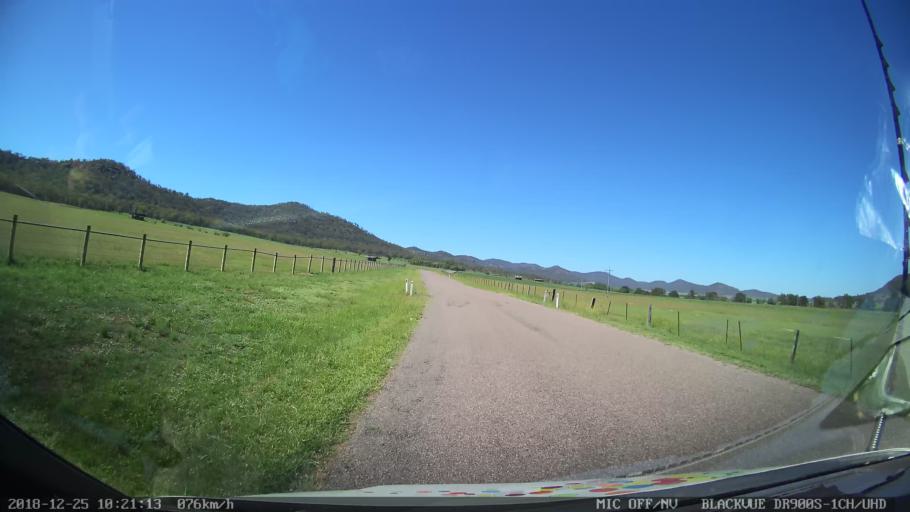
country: AU
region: New South Wales
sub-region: Muswellbrook
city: Denman
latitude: -32.3650
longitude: 150.5425
